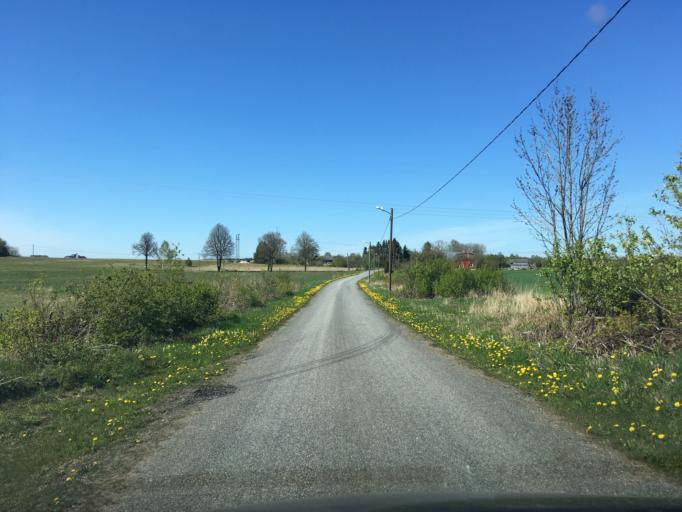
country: EE
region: Harju
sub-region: Raasiku vald
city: Arukula
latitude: 59.2678
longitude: 25.0946
